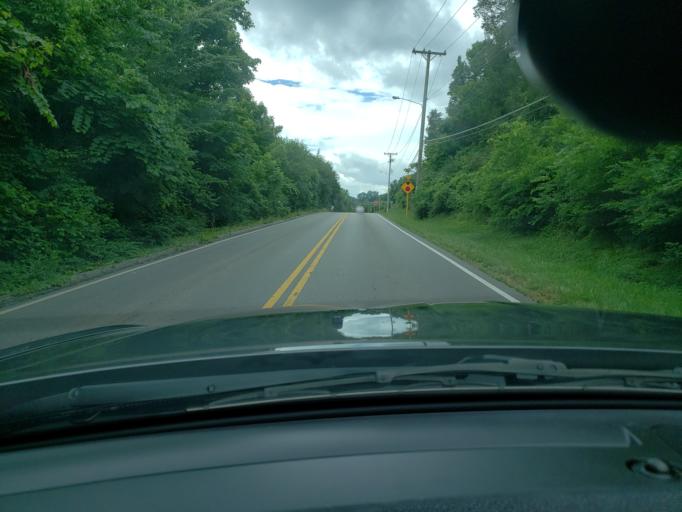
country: US
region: Tennessee
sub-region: Williamson County
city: Nolensville
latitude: 36.0237
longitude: -86.6801
